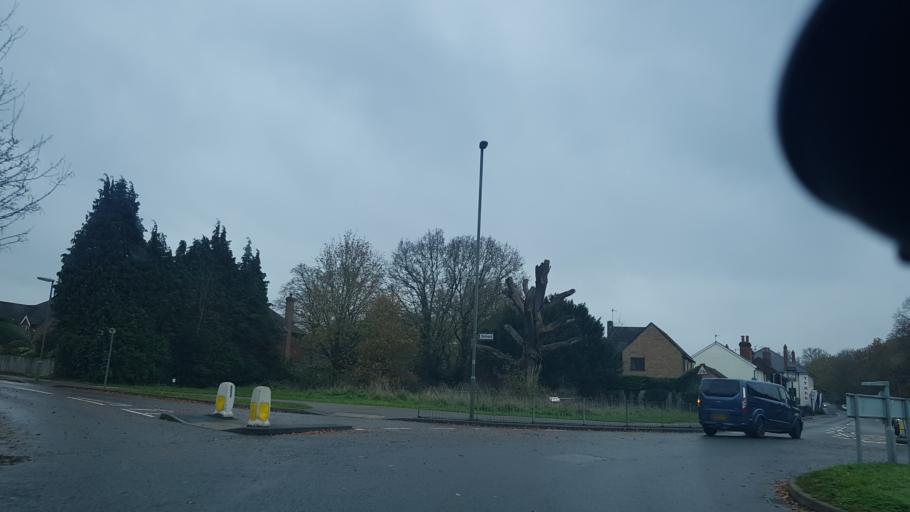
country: GB
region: England
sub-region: Surrey
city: Guildford
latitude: 51.2558
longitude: -0.5482
